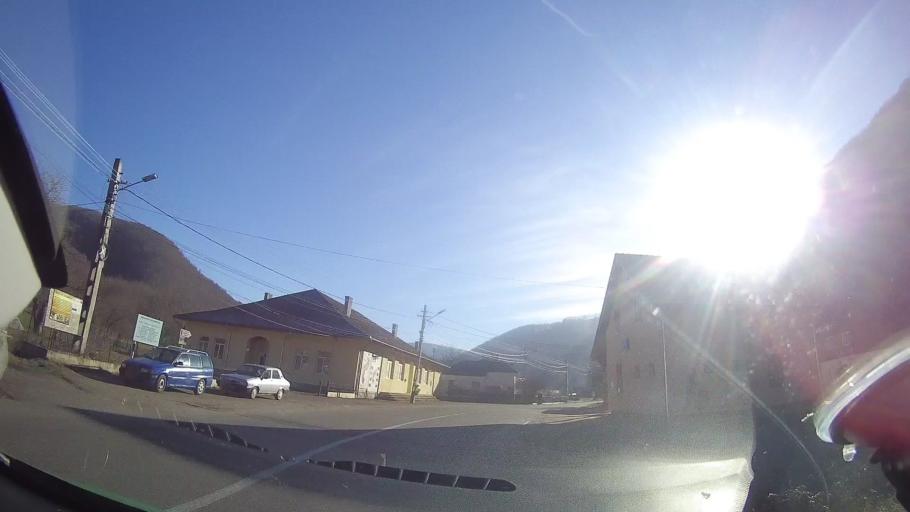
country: RO
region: Bihor
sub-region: Comuna Bulz
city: Bulz
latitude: 46.9130
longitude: 22.6757
